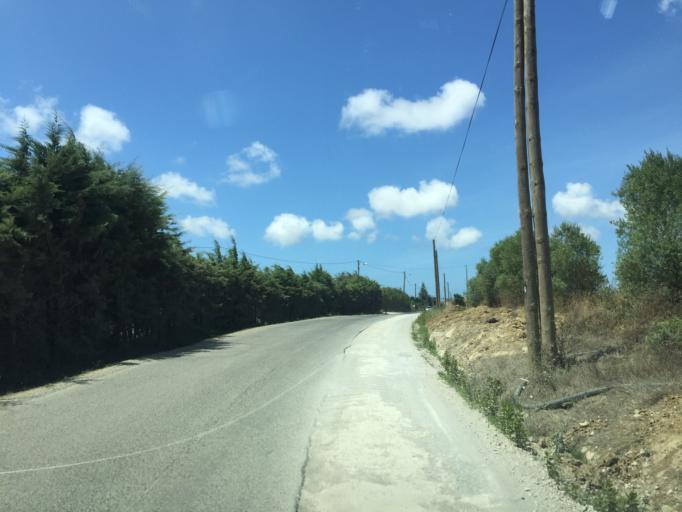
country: PT
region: Lisbon
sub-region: Lourinha
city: Lourinha
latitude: 39.2779
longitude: -9.2536
